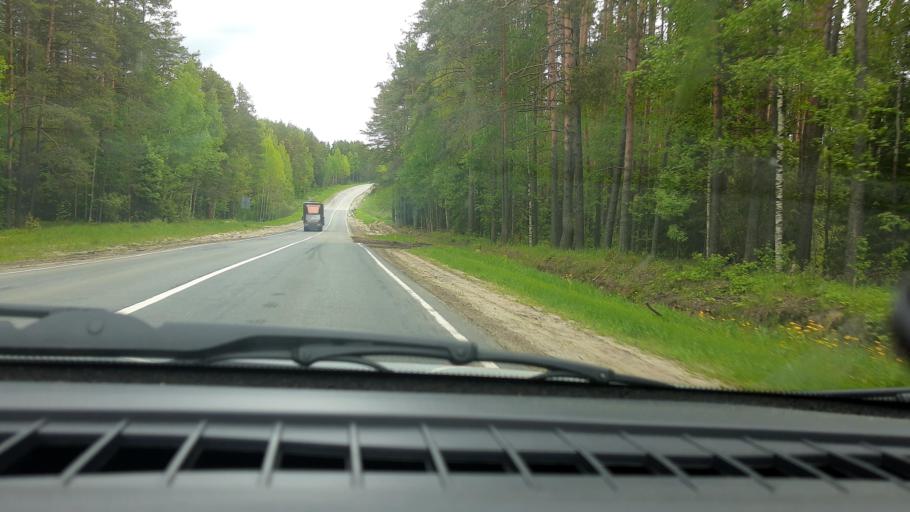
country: RU
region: Nizjnij Novgorod
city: Krasnyye Baki
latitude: 56.9903
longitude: 45.1160
